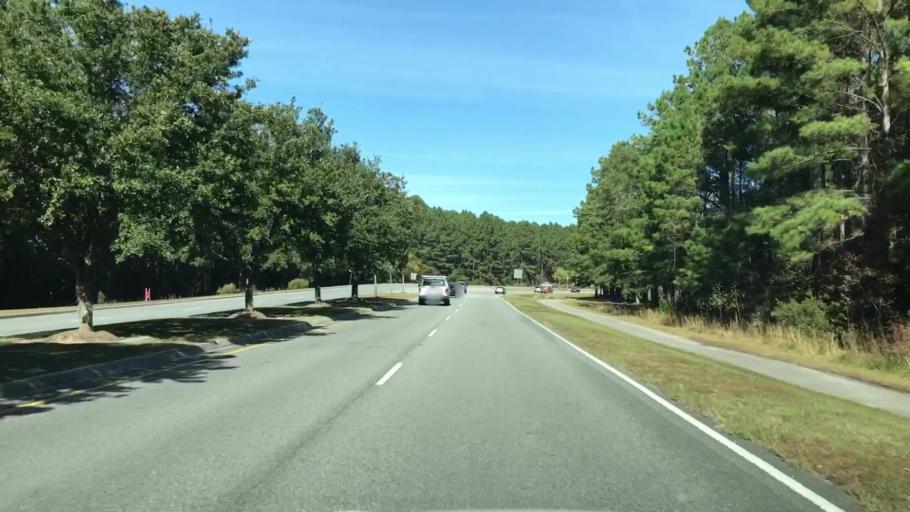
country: US
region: South Carolina
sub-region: Beaufort County
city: Bluffton
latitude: 32.2773
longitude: -80.9133
